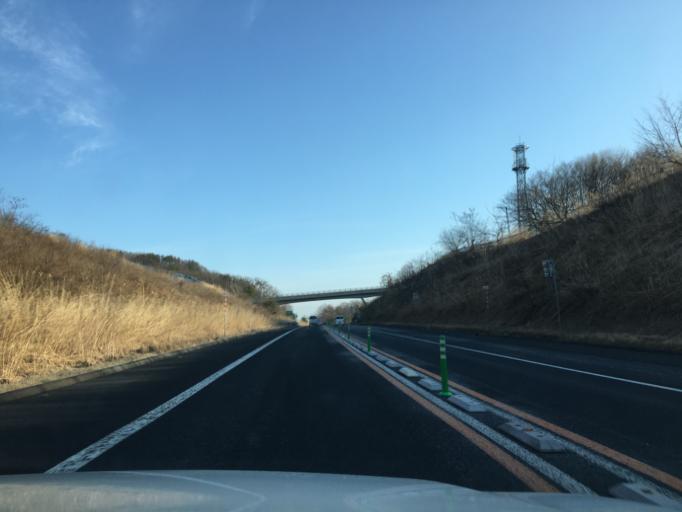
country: JP
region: Yamagata
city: Sagae
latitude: 38.3963
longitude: 140.2125
